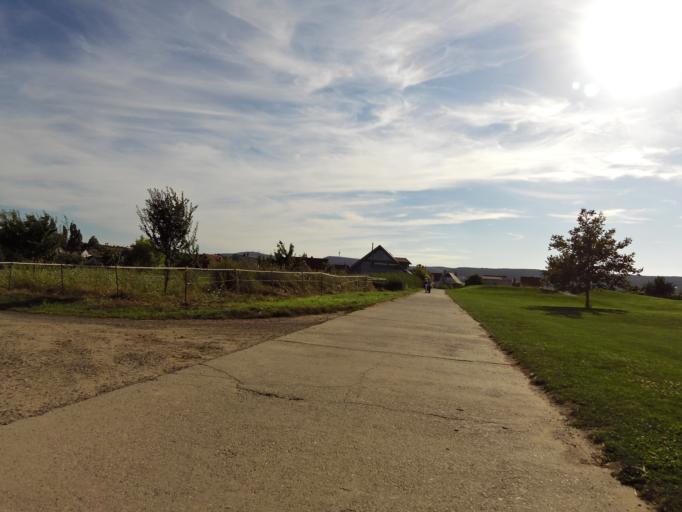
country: DE
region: Rheinland-Pfalz
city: Dackenheim
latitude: 49.5242
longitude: 8.1858
